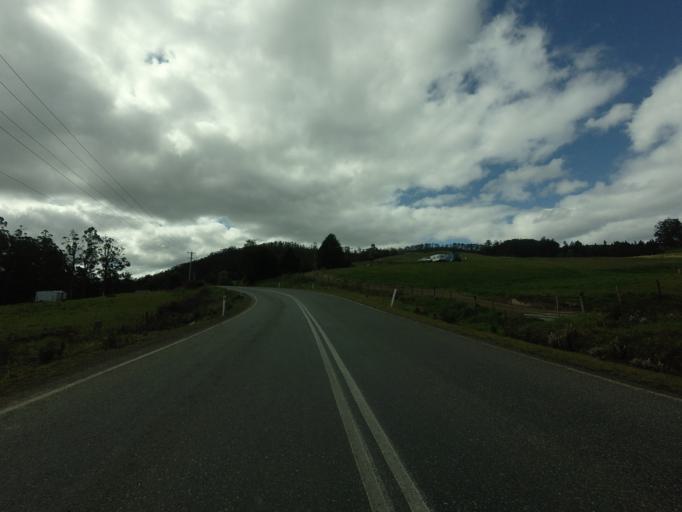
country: AU
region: Tasmania
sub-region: Huon Valley
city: Cygnet
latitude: -43.2881
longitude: 147.0108
